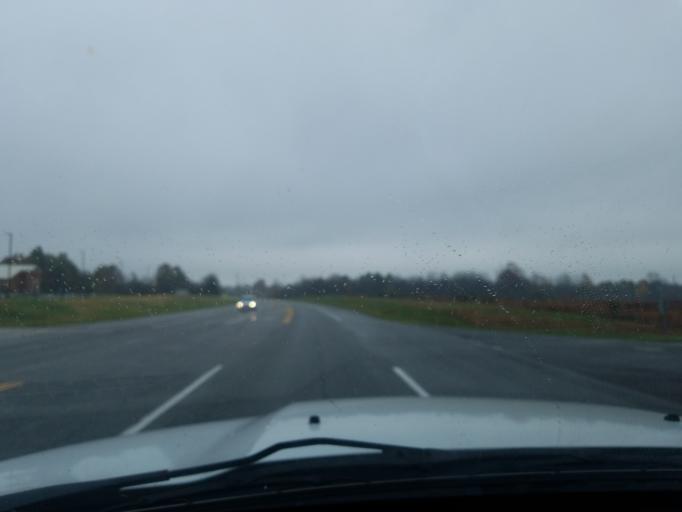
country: US
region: Kentucky
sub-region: Larue County
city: Hodgenville
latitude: 37.5514
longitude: -85.7288
